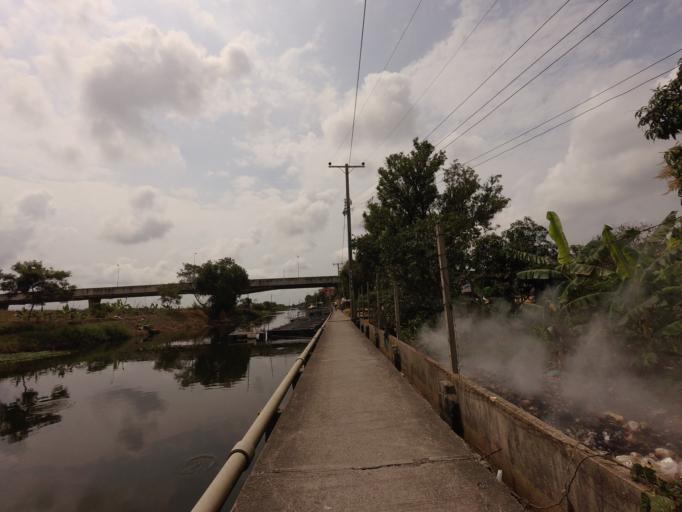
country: TH
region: Bangkok
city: Lat Krabang
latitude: 13.6730
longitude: 100.7255
